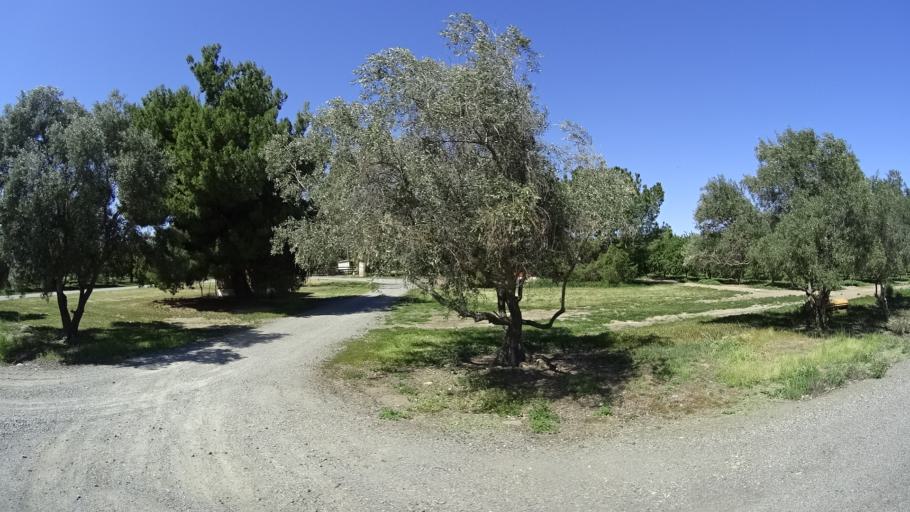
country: US
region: California
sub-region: Glenn County
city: Orland
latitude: 39.6828
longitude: -122.1221
